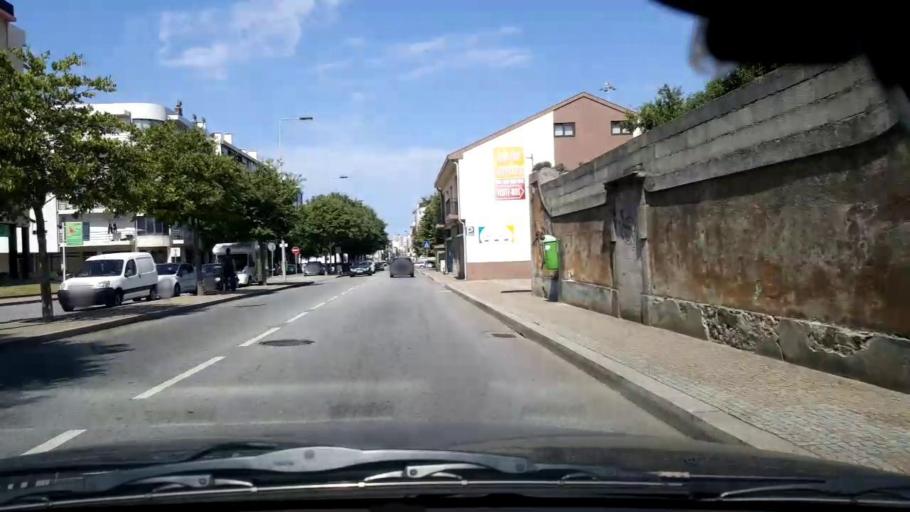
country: PT
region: Porto
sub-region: Povoa de Varzim
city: Povoa de Varzim
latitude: 41.3724
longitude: -8.7544
